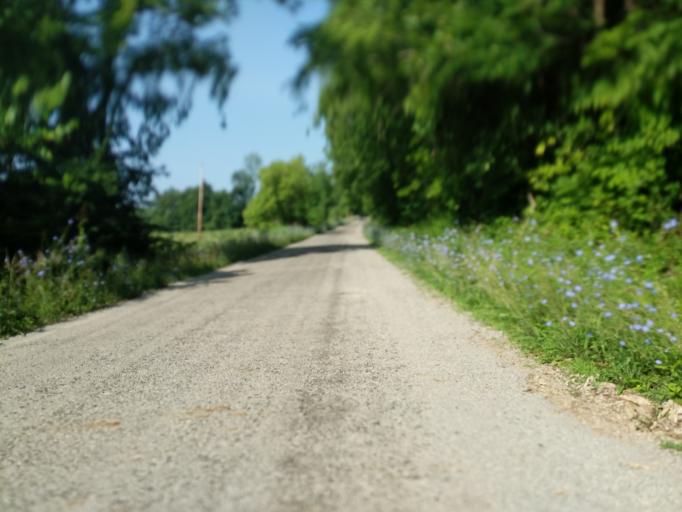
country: US
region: Ohio
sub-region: Athens County
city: Athens
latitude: 39.3429
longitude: -82.1171
